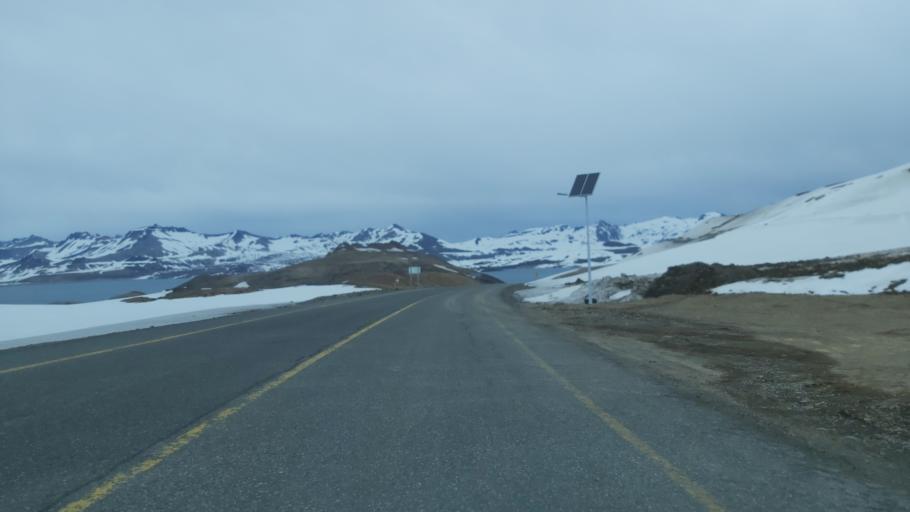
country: CL
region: Maule
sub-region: Provincia de Linares
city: Colbun
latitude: -36.0108
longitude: -70.4829
